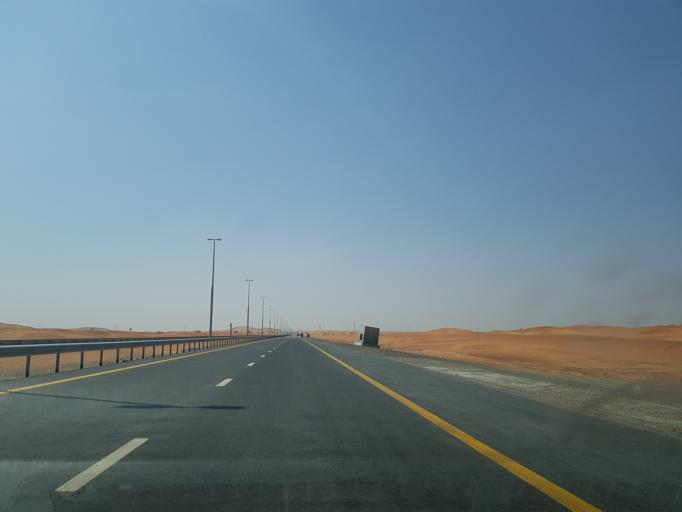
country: AE
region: Ash Shariqah
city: Adh Dhayd
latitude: 25.2407
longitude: 55.8824
